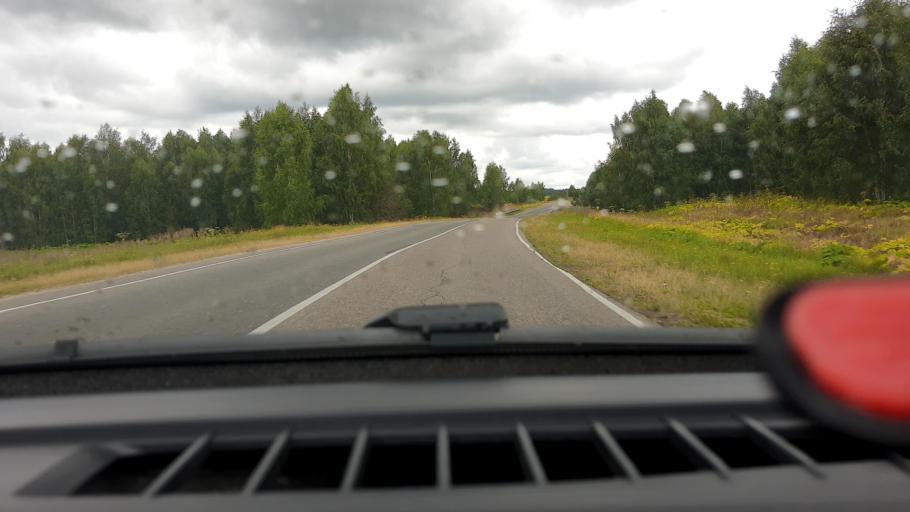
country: RU
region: Nizjnij Novgorod
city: Sitniki
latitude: 56.4955
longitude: 44.0076
